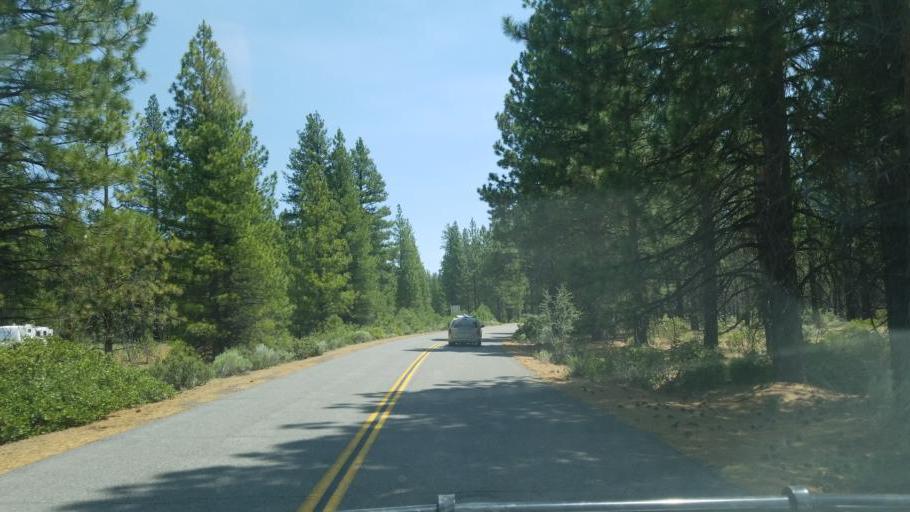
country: US
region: California
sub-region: Lassen County
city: Susanville
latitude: 40.5674
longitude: -120.8400
